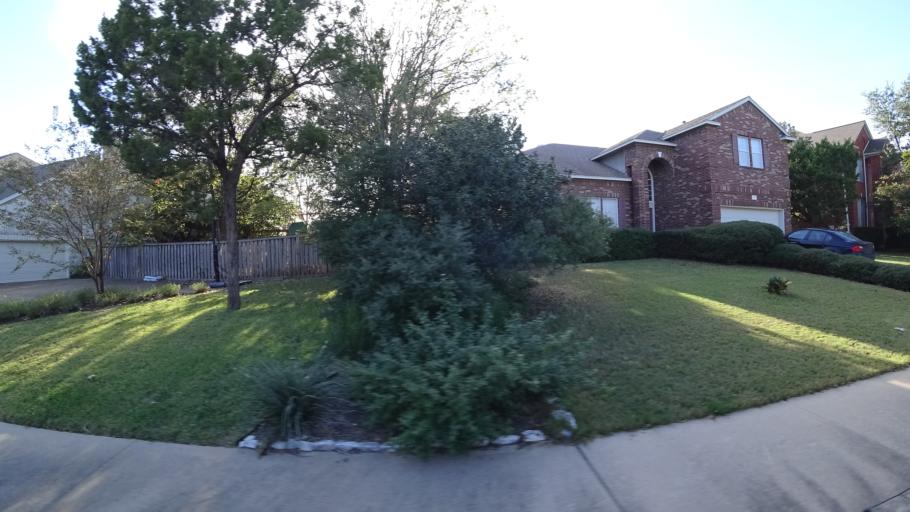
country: US
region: Texas
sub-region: Williamson County
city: Jollyville
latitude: 30.3987
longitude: -97.7728
